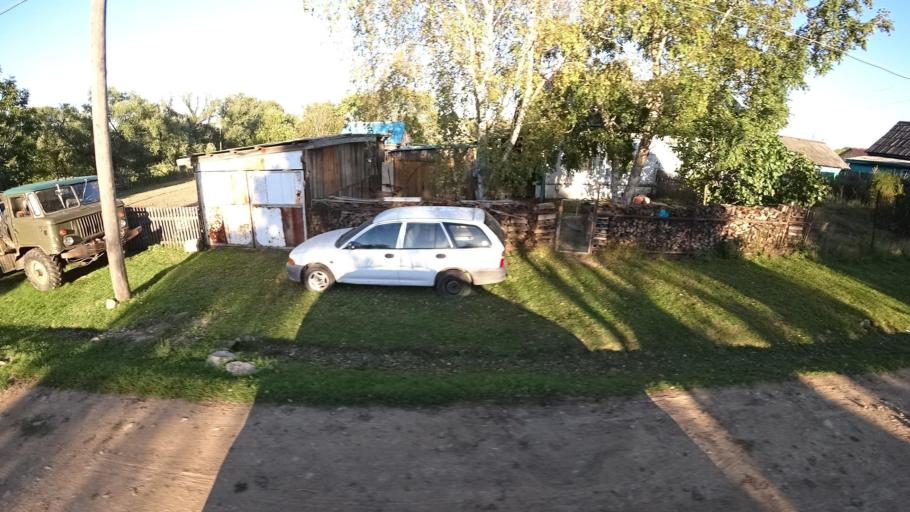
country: RU
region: Primorskiy
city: Kirovskiy
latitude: 44.8335
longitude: 133.5756
